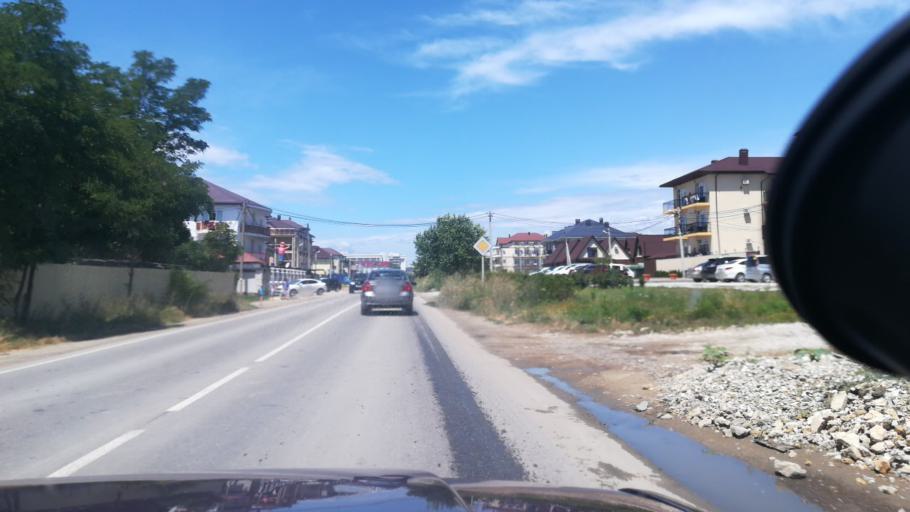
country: RU
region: Krasnodarskiy
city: Vityazevo
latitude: 44.9601
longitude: 37.2954
